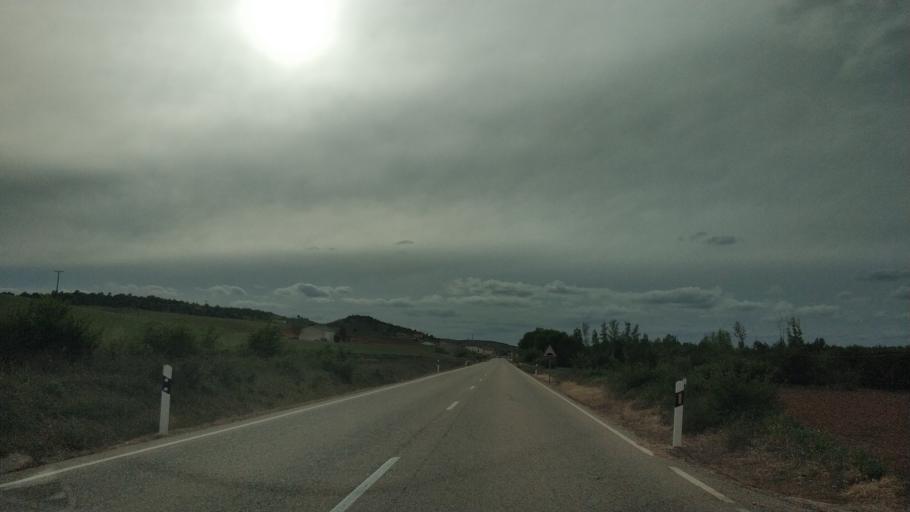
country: ES
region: Castille and Leon
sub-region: Provincia de Soria
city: Valdenebro
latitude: 41.5678
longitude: -3.0035
